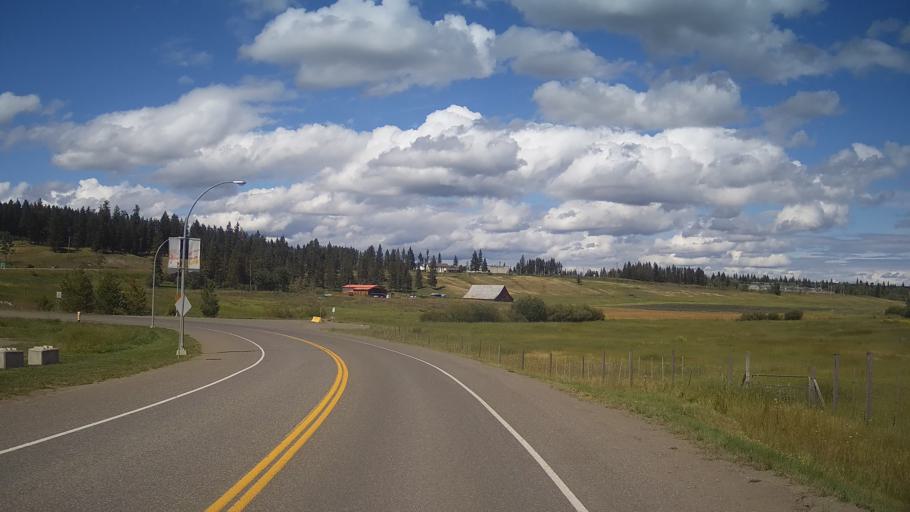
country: CA
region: British Columbia
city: Cache Creek
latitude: 51.6492
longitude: -121.2937
